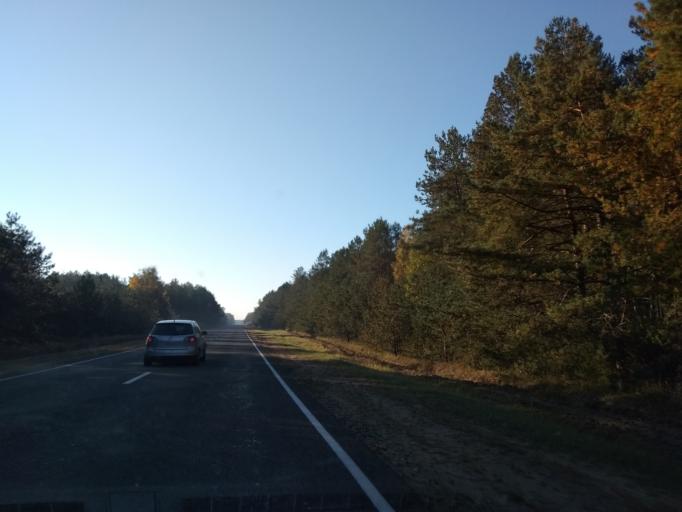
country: BY
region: Brest
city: Kobryn
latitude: 52.0864
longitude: 24.2801
